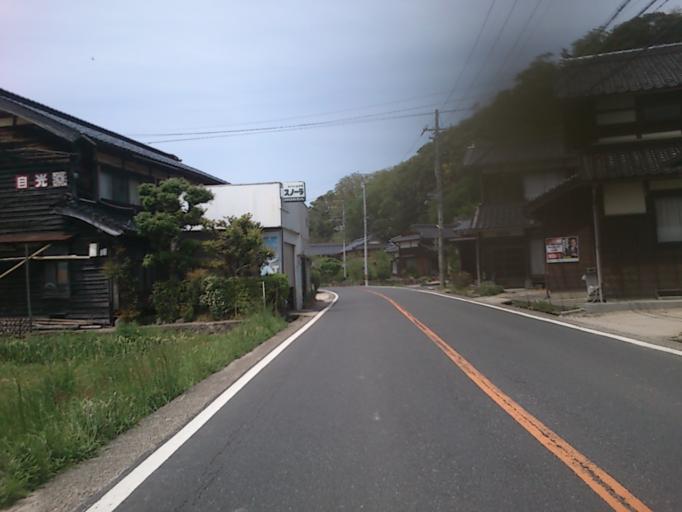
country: JP
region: Kyoto
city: Miyazu
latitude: 35.6833
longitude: 135.0995
